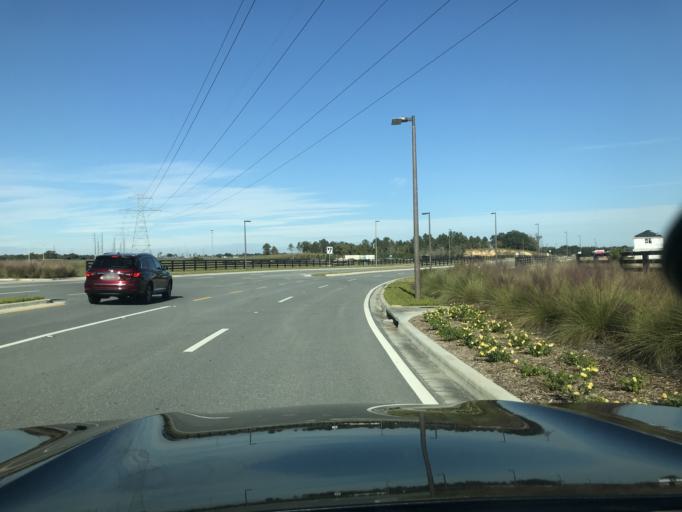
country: US
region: Florida
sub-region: Orange County
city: Oakland
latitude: 28.4778
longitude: -81.6271
